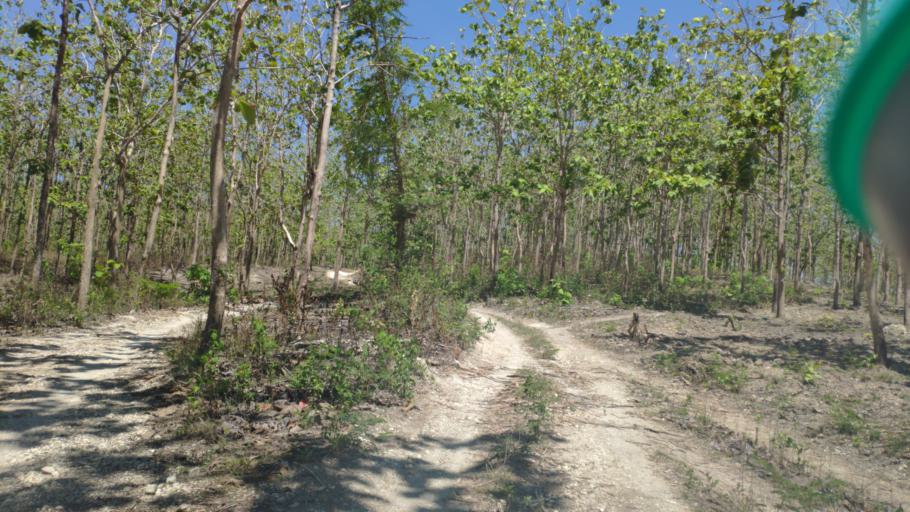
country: ID
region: Central Java
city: Suruhan
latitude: -7.0068
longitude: 111.5277
